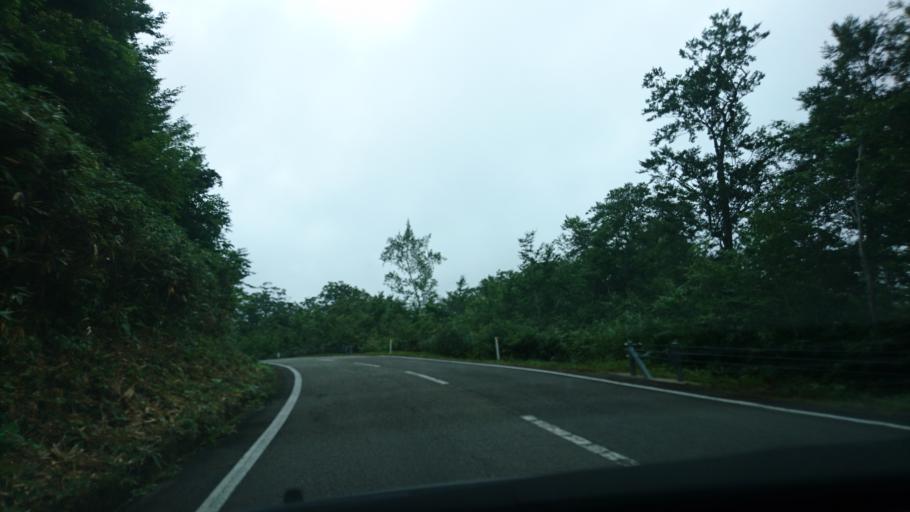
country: JP
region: Akita
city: Yuzawa
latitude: 38.9807
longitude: 140.7437
